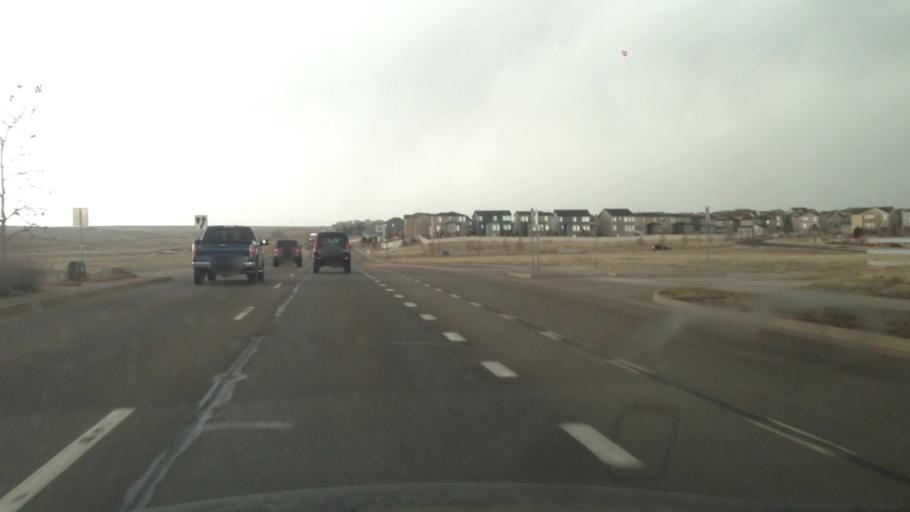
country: US
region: Colorado
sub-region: Douglas County
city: Parker
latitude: 39.4932
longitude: -104.7766
